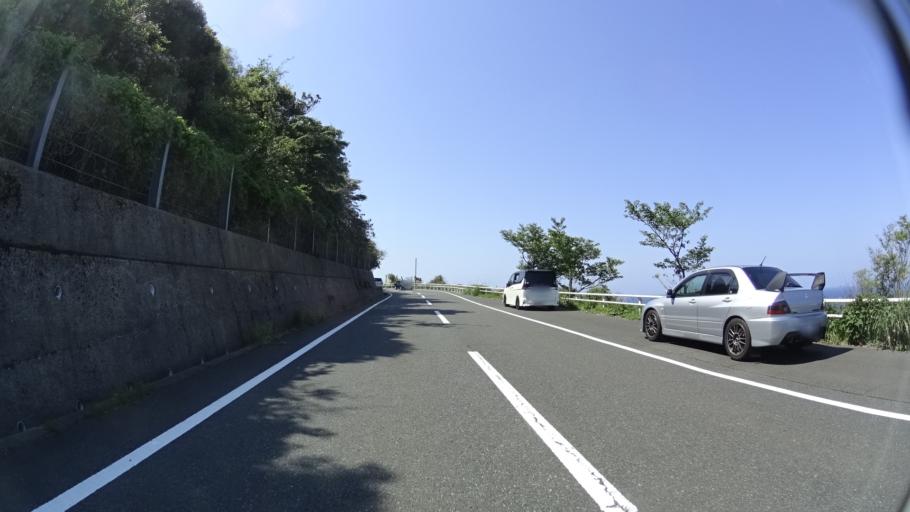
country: JP
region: Kyoto
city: Miyazu
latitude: 35.7588
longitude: 135.2444
